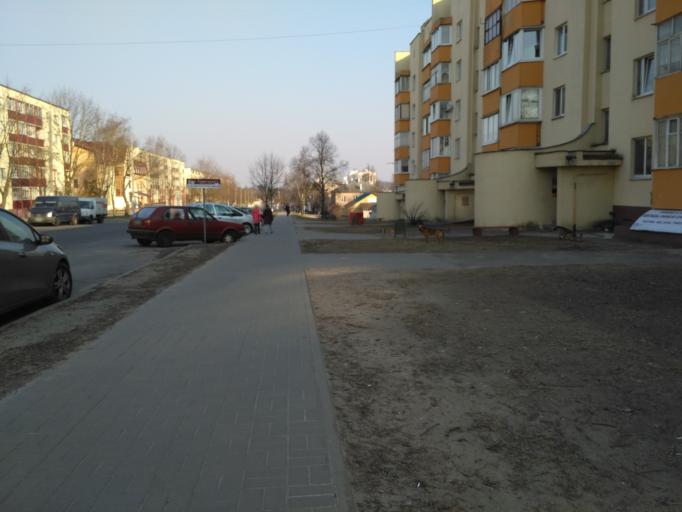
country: BY
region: Minsk
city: Zaslawye
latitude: 54.0117
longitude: 27.2664
